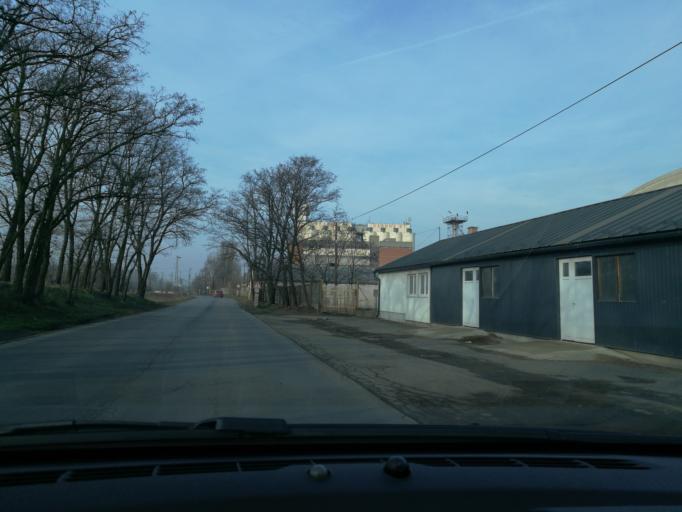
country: HU
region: Szabolcs-Szatmar-Bereg
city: Nyiregyhaza
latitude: 47.9337
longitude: 21.7142
